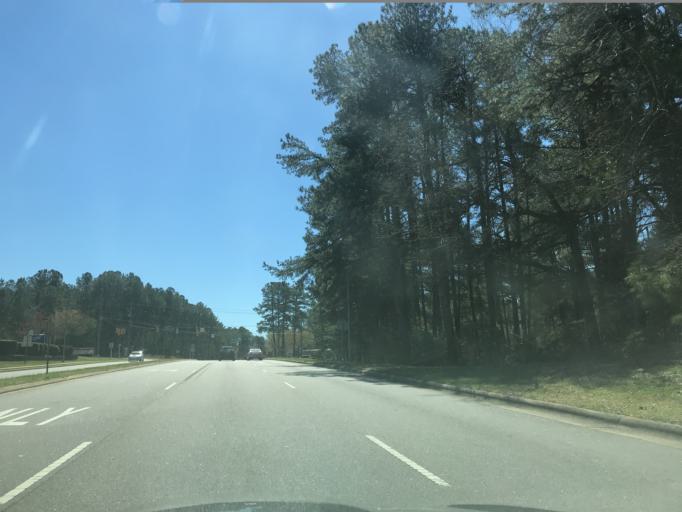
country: US
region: North Carolina
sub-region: Wake County
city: Garner
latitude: 35.6940
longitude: -78.6368
